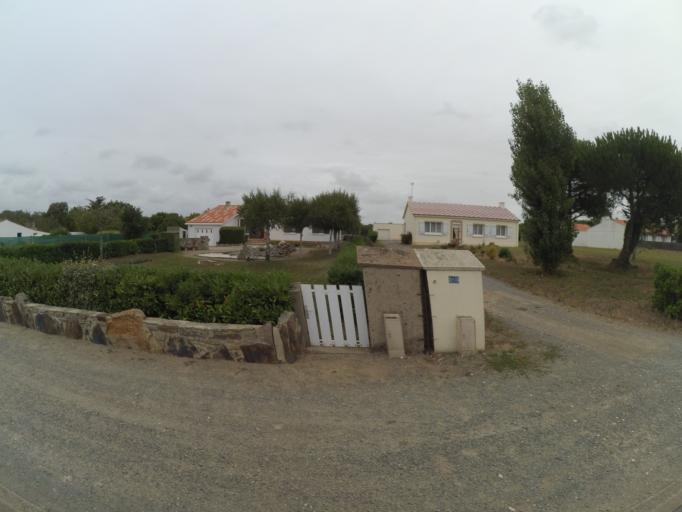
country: FR
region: Pays de la Loire
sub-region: Departement de la Vendee
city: Challans
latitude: 46.8581
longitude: -1.9030
